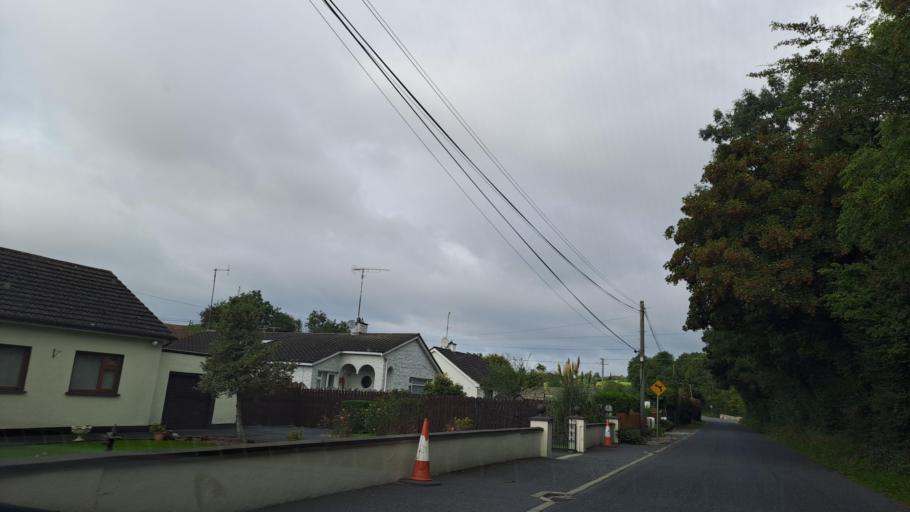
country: IE
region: Ulster
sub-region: County Monaghan
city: Carrickmacross
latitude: 53.9692
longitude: -6.7483
